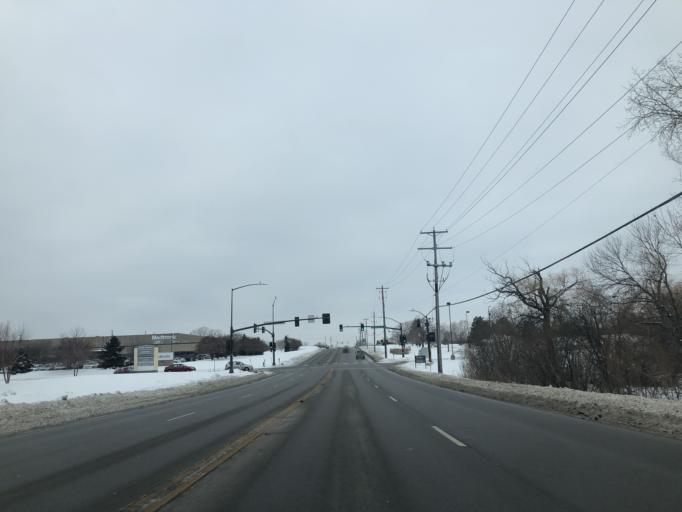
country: US
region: Minnesota
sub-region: Hennepin County
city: Osseo
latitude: 45.0946
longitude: -93.3947
